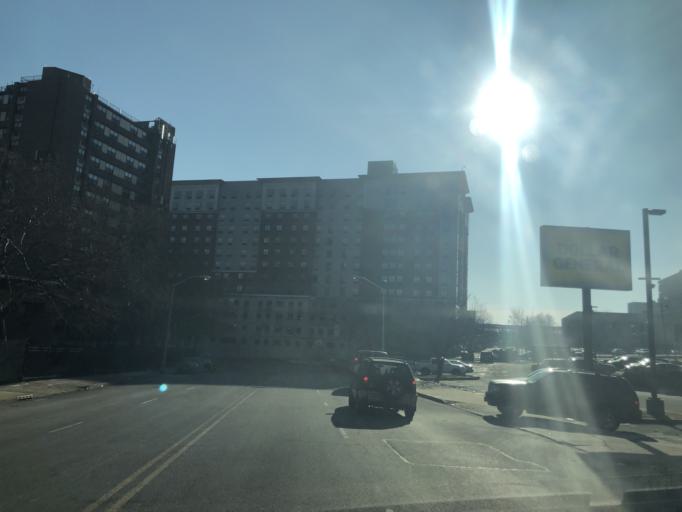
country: US
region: New Jersey
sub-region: Essex County
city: Newark
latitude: 40.7424
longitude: -74.1866
